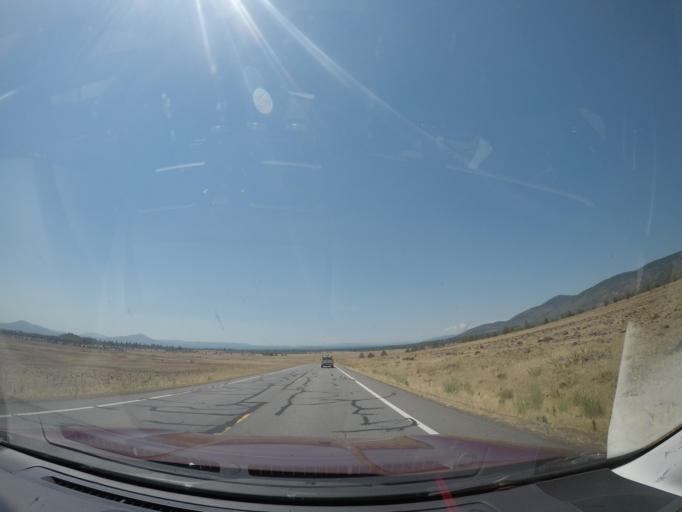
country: US
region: California
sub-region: Shasta County
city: Burney
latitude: 41.0979
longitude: -121.2872
